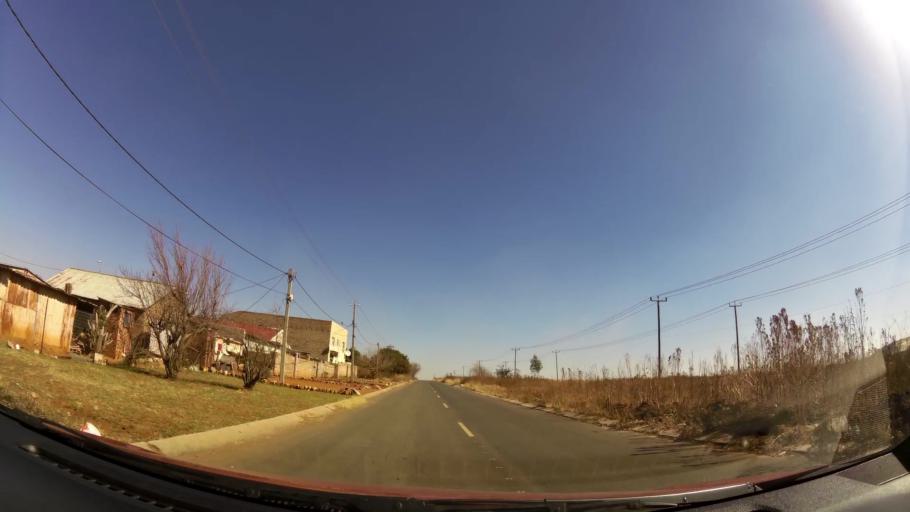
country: ZA
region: Gauteng
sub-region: City of Johannesburg Metropolitan Municipality
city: Soweto
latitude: -26.2157
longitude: 27.8371
